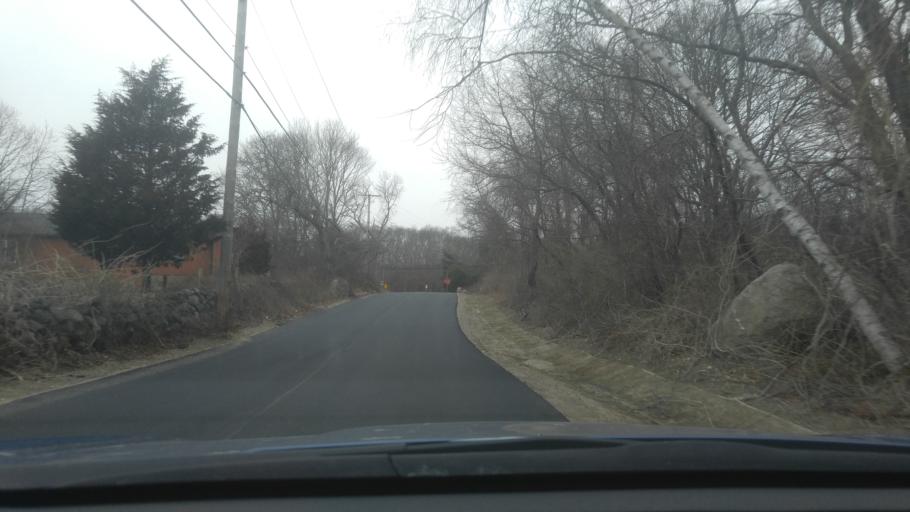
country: US
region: Rhode Island
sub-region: Washington County
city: Wakefield-Peacedale
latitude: 41.4076
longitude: -71.5306
